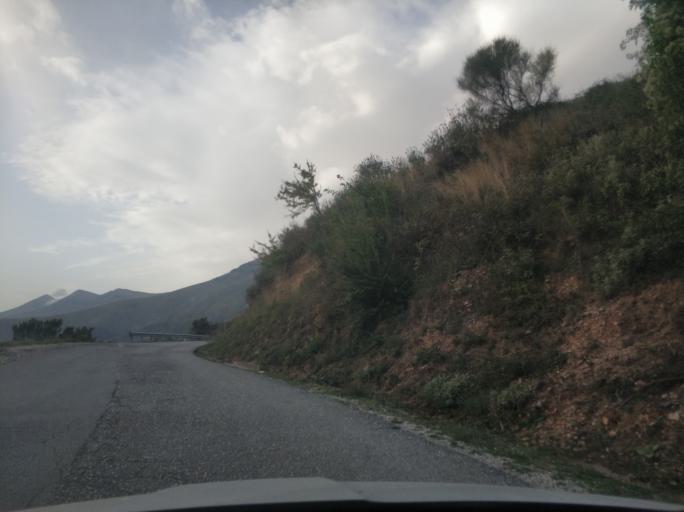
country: AL
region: Vlore
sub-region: Rrethi i Sarandes
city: Dhiver
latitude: 39.9220
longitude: 20.2037
